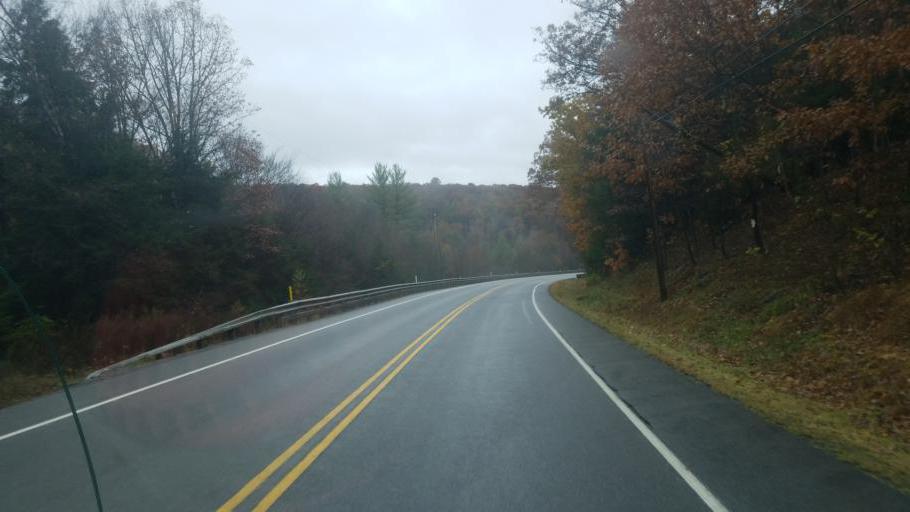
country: US
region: Pennsylvania
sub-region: Clearfield County
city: Shiloh
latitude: 41.1165
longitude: -78.1561
